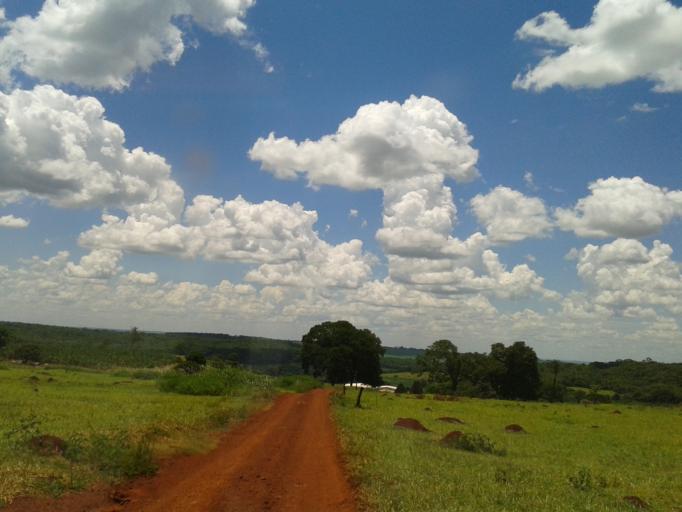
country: BR
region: Minas Gerais
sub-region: Centralina
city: Centralina
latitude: -18.6929
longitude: -49.1973
